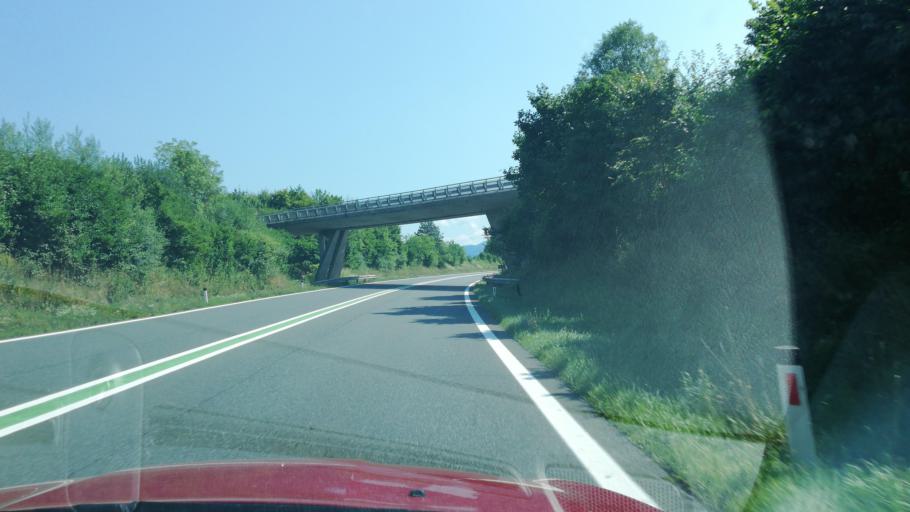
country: AT
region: Carinthia
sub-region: Klagenfurt am Woerthersee
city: Klagenfurt am Woerthersee
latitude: 46.6633
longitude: 14.3001
